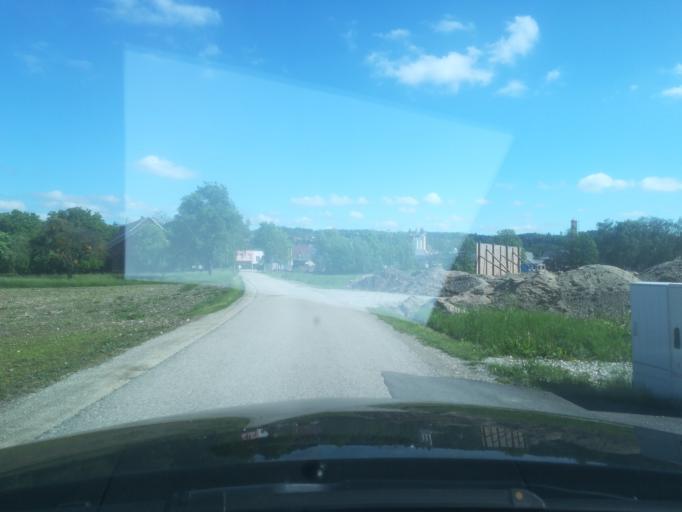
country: AT
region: Upper Austria
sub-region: Politischer Bezirk Perg
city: Perg
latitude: 48.2446
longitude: 14.6246
